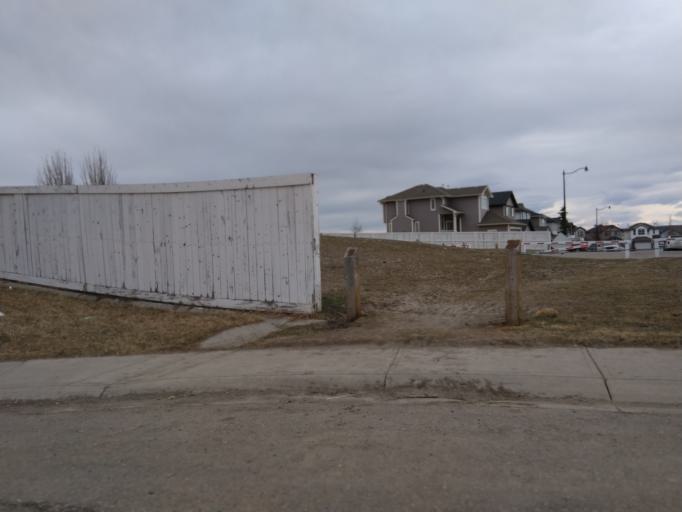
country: CA
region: Alberta
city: Calgary
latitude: 51.1688
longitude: -114.1089
